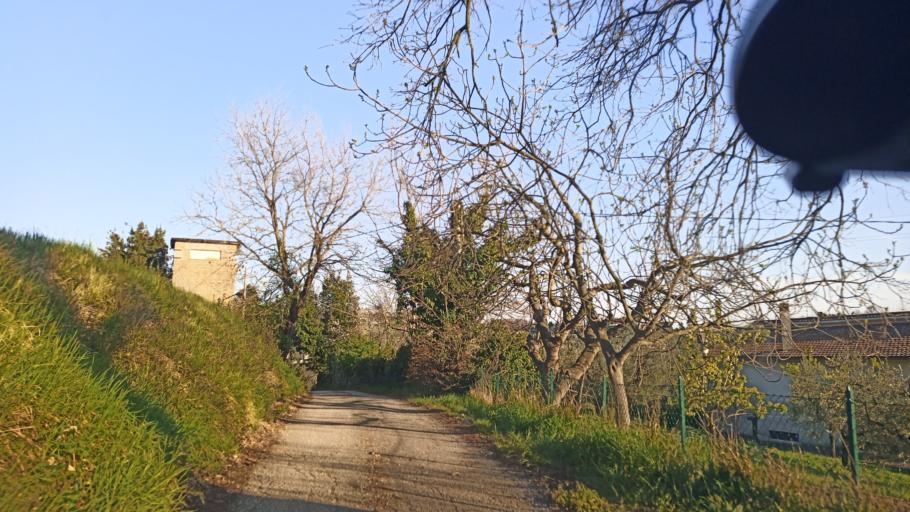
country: IT
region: Latium
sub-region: Provincia di Rieti
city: Poggio Mirteto
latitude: 42.2636
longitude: 12.6634
